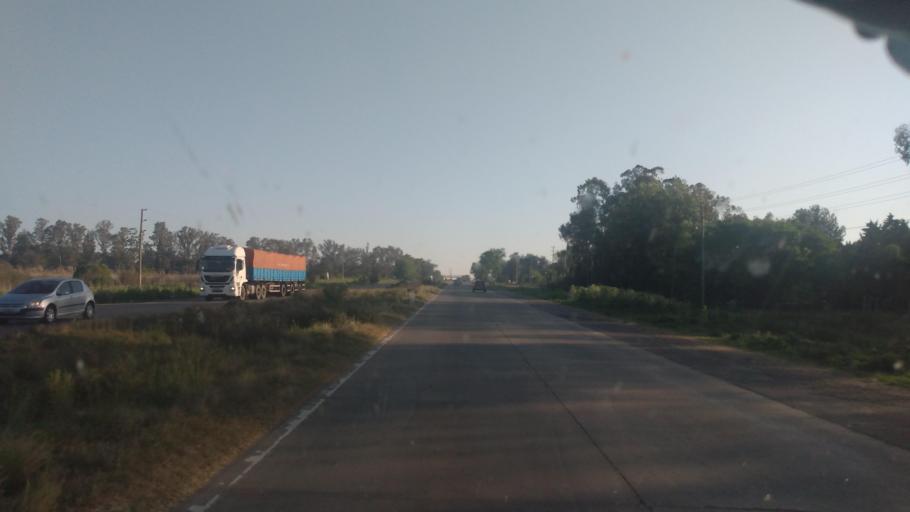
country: AR
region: Buenos Aires
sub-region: Partido de Campana
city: Campana
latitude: -34.2579
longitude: -58.9655
